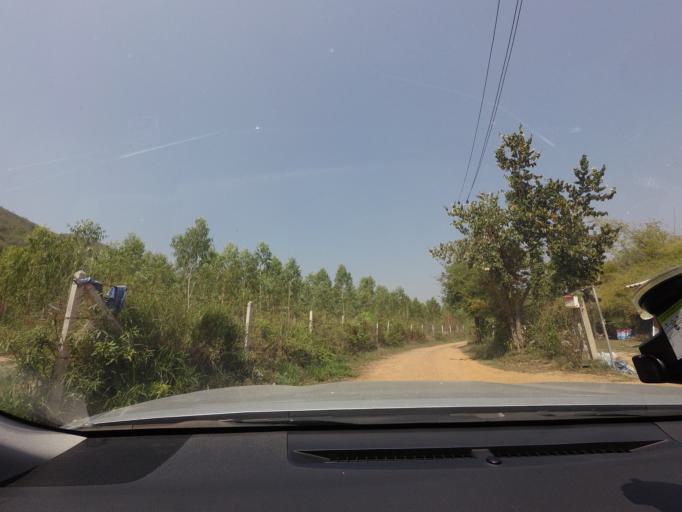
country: TH
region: Prachuap Khiri Khan
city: Prachuap Khiri Khan
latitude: 11.9318
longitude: 99.8188
